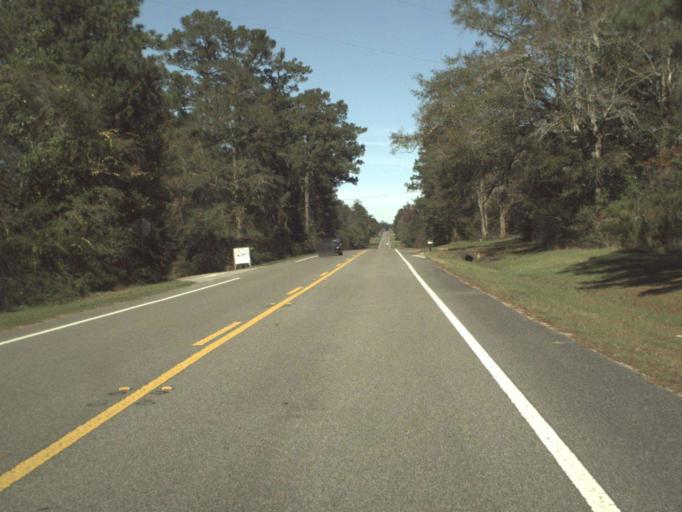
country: US
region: Florida
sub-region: Okaloosa County
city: Crestview
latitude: 30.9699
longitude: -86.6314
